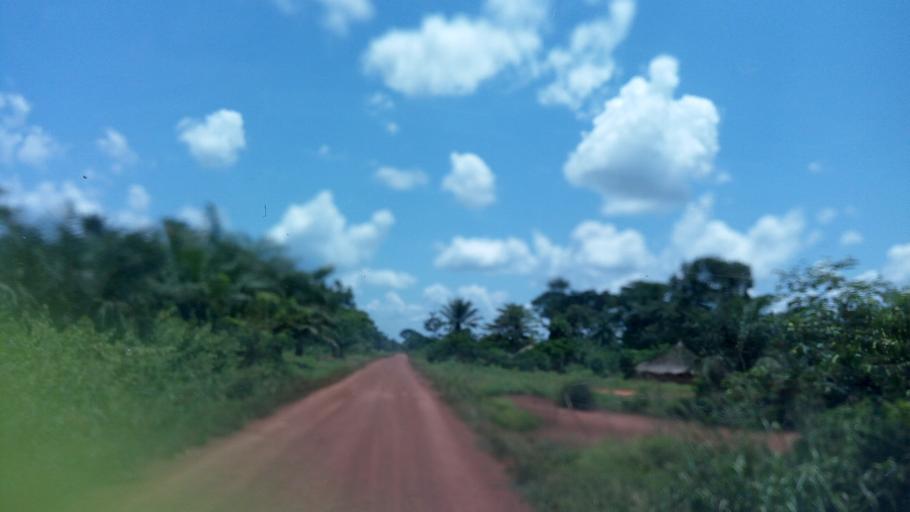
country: CD
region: Equateur
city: Gemena
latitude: 3.5242
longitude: 19.3624
